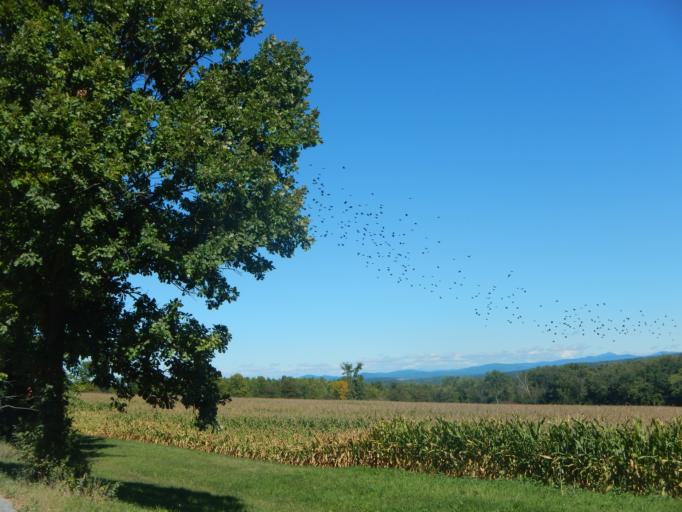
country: US
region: Vermont
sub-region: Addison County
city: Middlebury (village)
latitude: 44.0193
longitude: -73.2564
